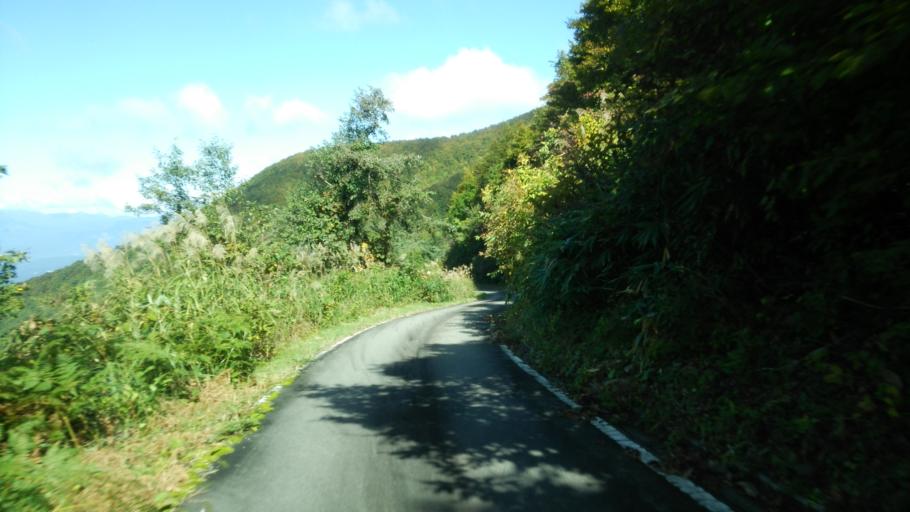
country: JP
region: Fukushima
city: Kitakata
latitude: 37.6117
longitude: 139.9914
